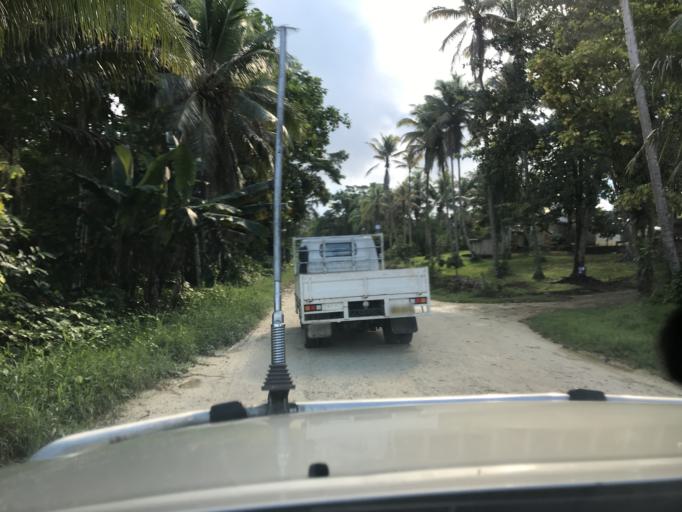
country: SB
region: Malaita
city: Auki
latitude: -8.6933
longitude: 160.6966
